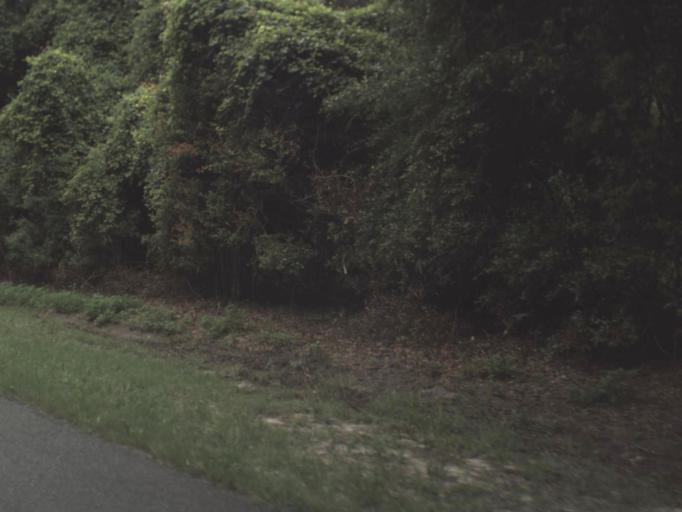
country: US
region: Florida
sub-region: Alachua County
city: Newberry
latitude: 29.6003
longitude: -82.5741
